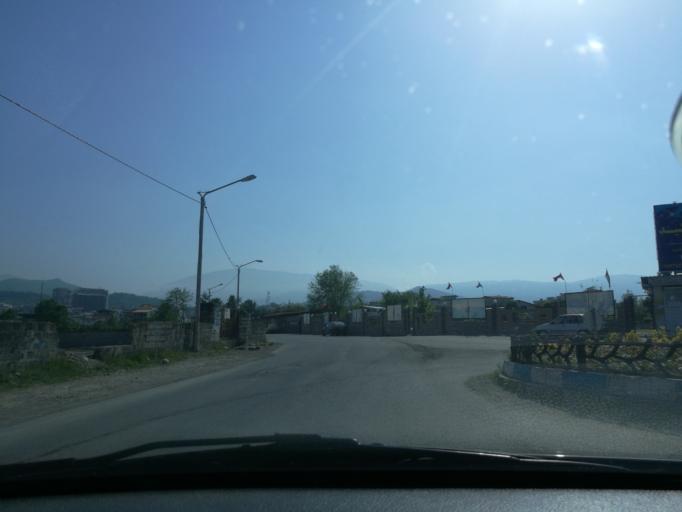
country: IR
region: Mazandaran
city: Chalus
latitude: 36.6590
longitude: 51.4336
